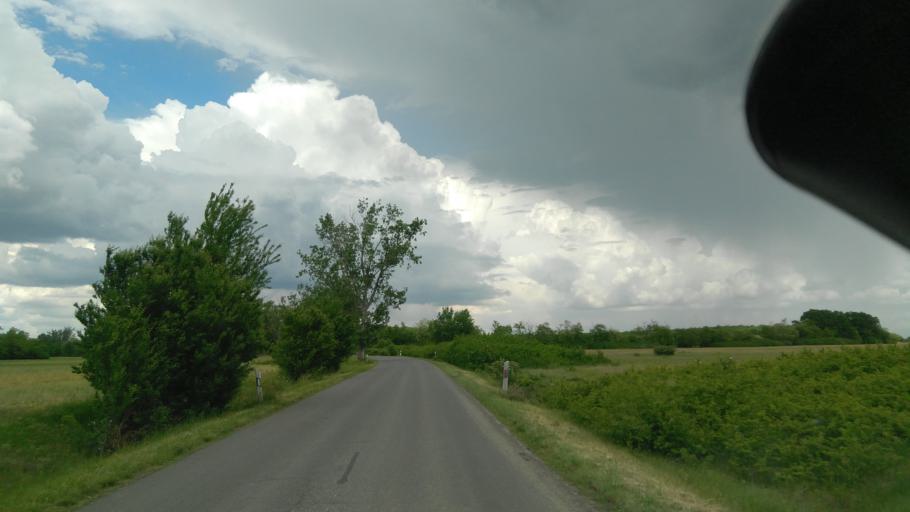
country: HU
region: Bekes
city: Bucsa
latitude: 47.1566
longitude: 21.0787
